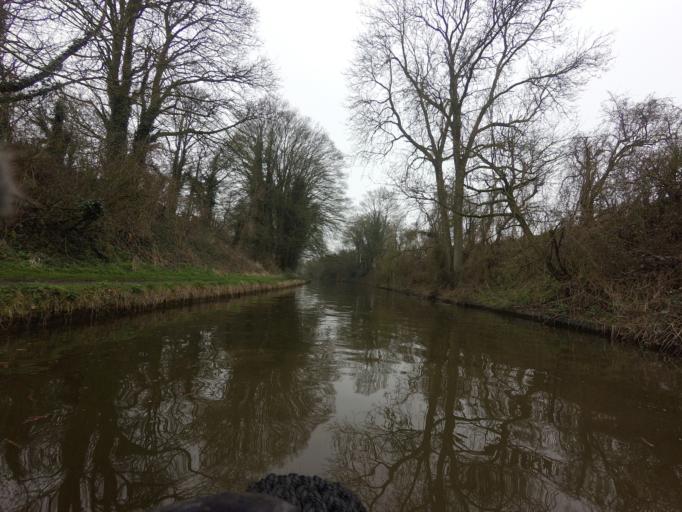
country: GB
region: England
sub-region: Hertfordshire
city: Tring
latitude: 51.7942
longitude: -0.6212
